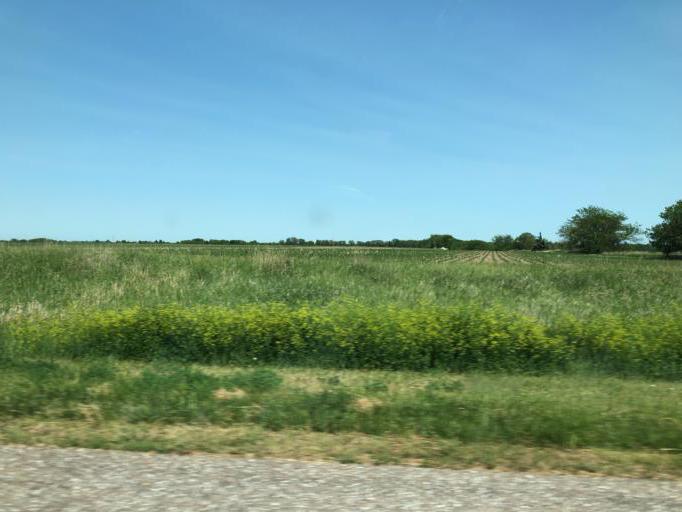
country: US
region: Nebraska
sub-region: Fillmore County
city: Geneva
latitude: 40.3867
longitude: -97.5772
